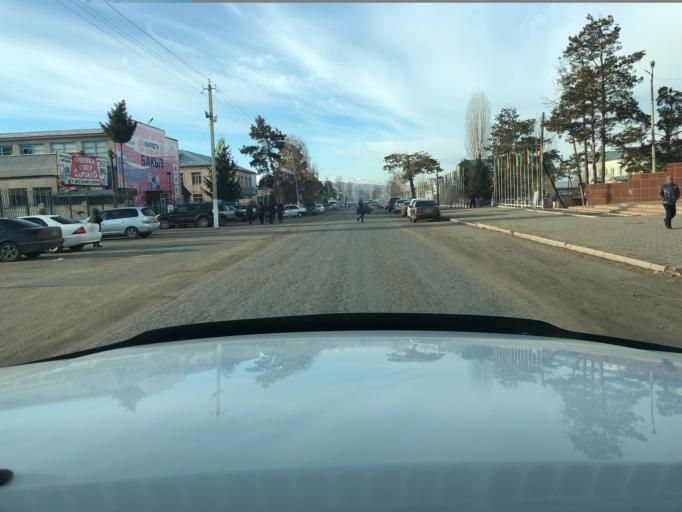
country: KG
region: Ysyk-Koel
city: Pokrovka
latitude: 42.3413
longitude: 78.0029
